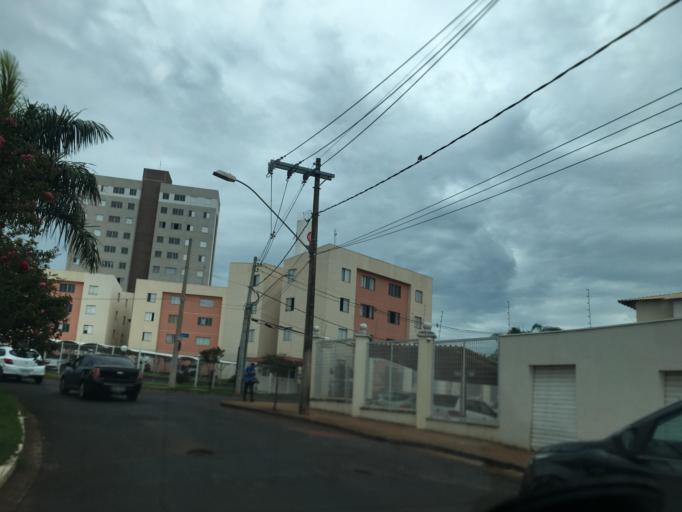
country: BR
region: Minas Gerais
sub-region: Uberlandia
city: Uberlandia
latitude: -18.8820
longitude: -48.2432
